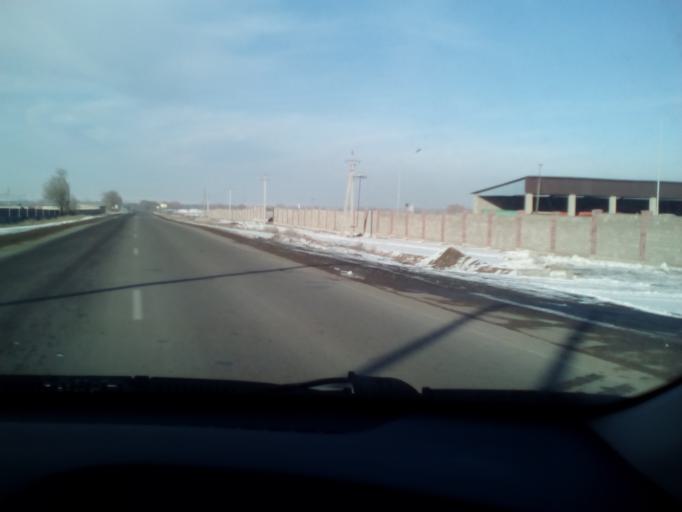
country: KZ
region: Almaty Oblysy
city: Burunday
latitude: 43.2034
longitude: 76.4149
